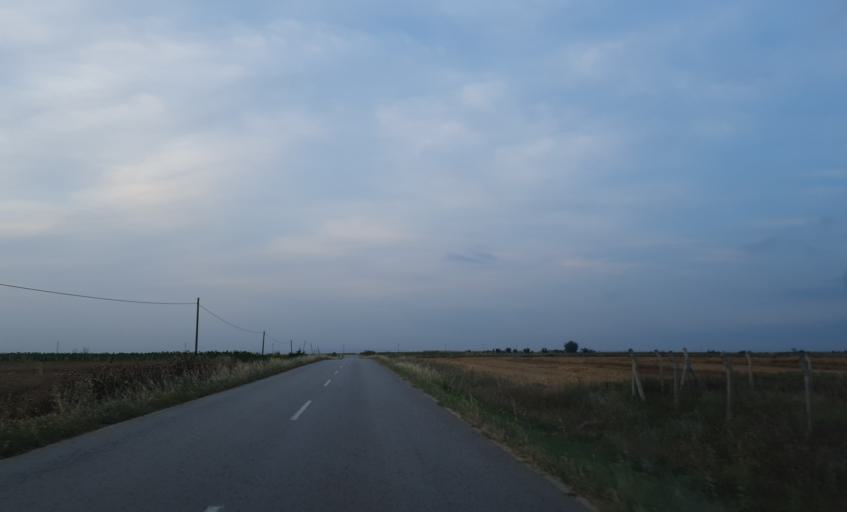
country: TR
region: Kirklareli
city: Buyukkaristiran
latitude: 41.3196
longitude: 27.6054
